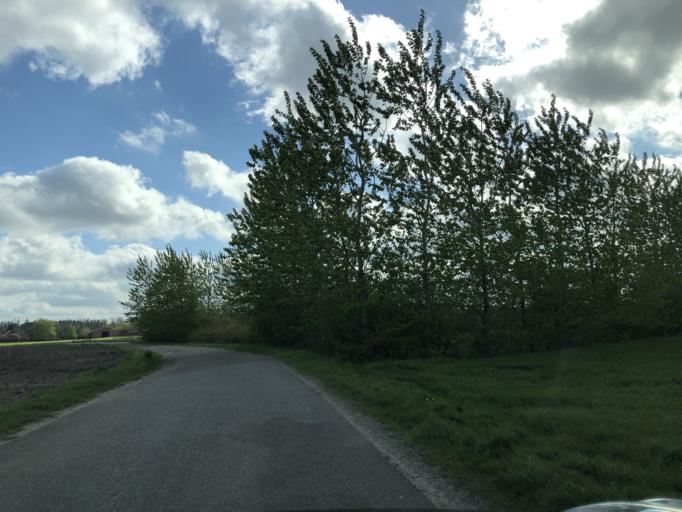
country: DK
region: Central Jutland
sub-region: Holstebro Kommune
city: Holstebro
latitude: 56.2696
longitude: 8.6491
